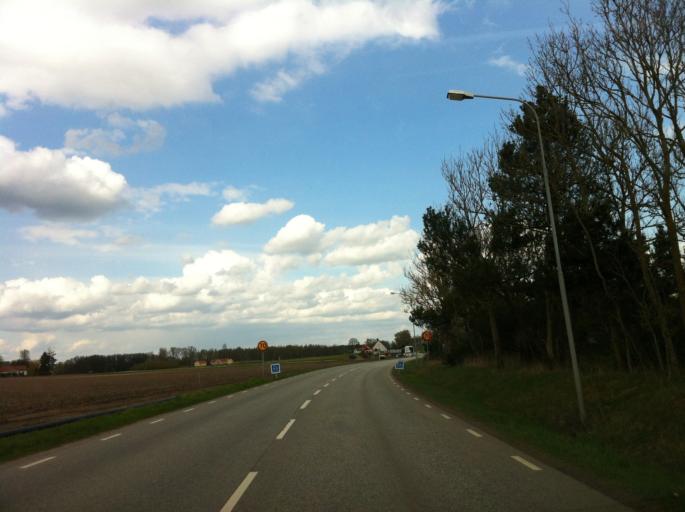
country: SE
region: Skane
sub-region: Svalovs Kommun
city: Teckomatorp
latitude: 55.8395
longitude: 13.1004
